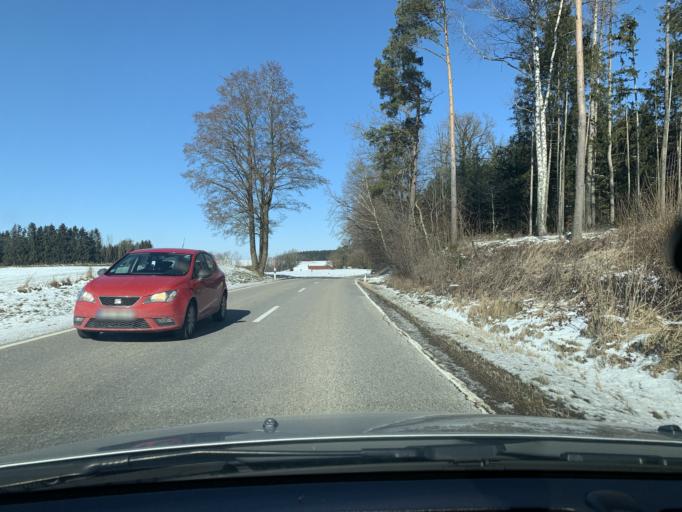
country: DE
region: Bavaria
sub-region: Upper Bavaria
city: Zangberg
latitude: 48.2997
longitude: 12.4327
